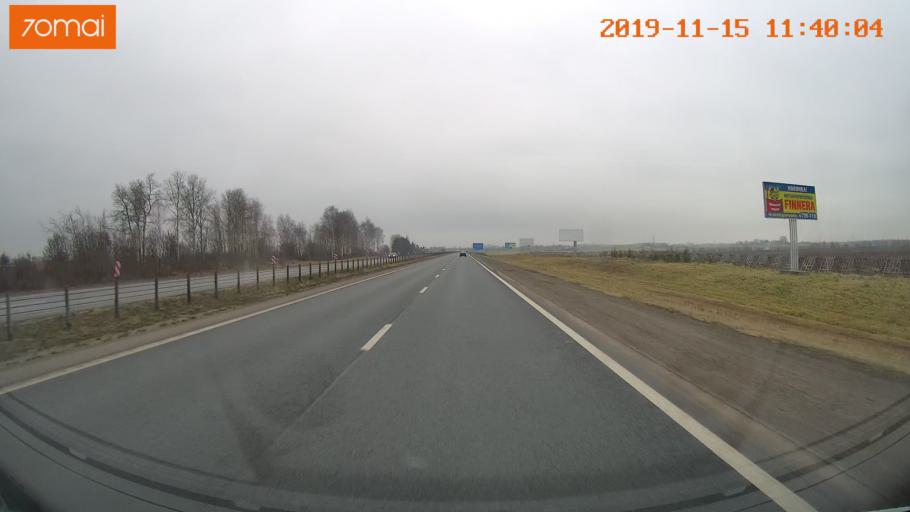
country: RU
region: Vologda
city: Molochnoye
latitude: 59.2122
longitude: 39.7414
